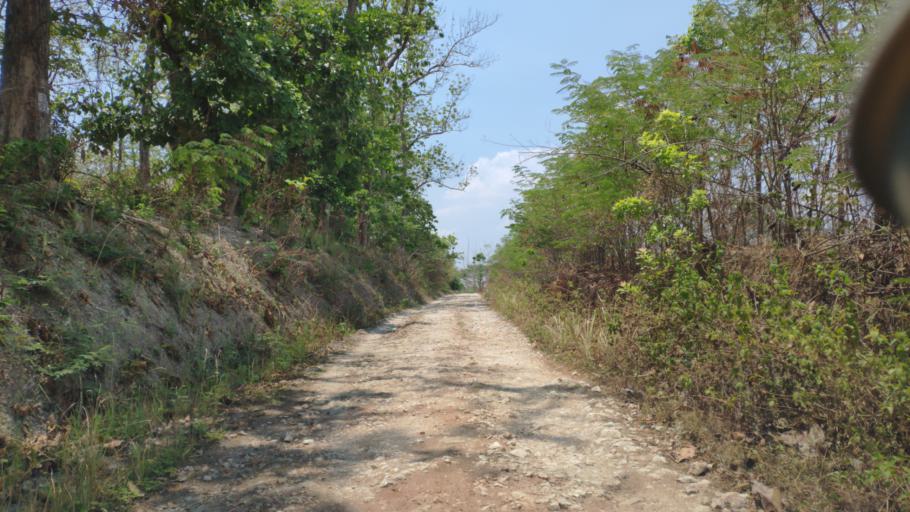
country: ID
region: Central Java
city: Botoh
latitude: -7.0735
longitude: 111.4802
